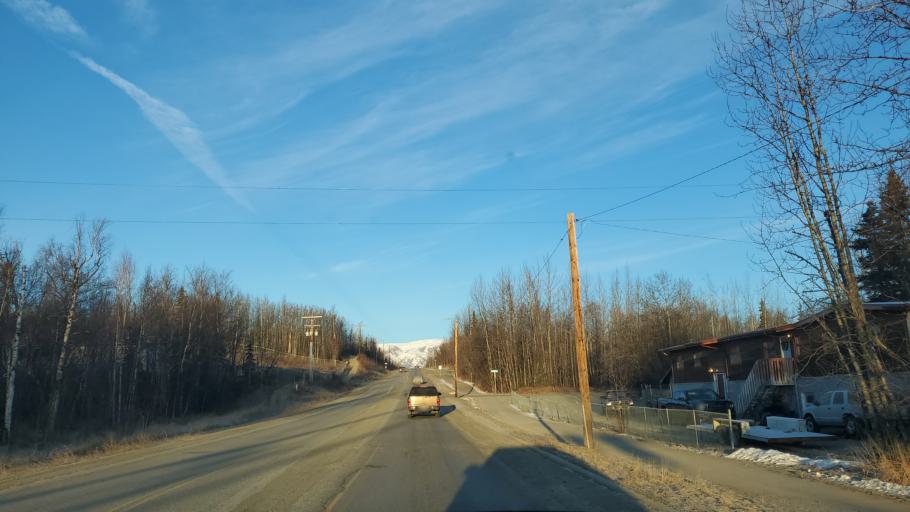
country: US
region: Alaska
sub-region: Matanuska-Susitna Borough
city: Wasilla
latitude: 61.5855
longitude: -149.4507
